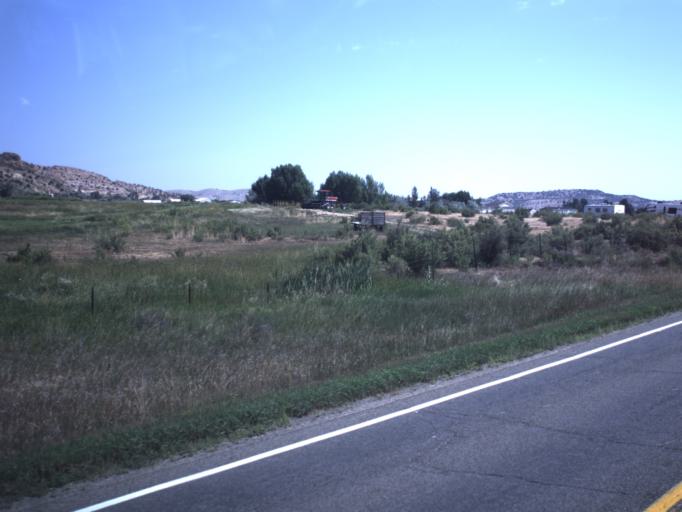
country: US
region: Utah
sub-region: Daggett County
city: Manila
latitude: 40.9896
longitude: -109.6910
